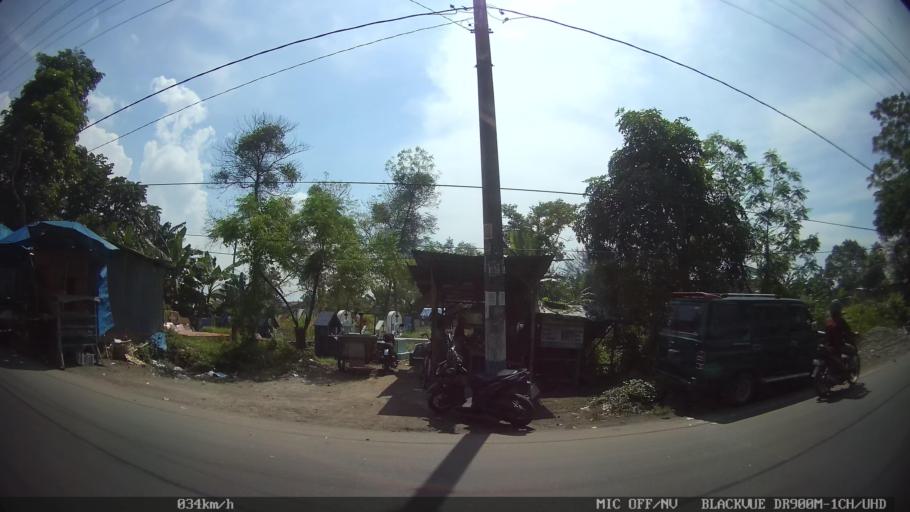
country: ID
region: North Sumatra
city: Medan
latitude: 3.6383
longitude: 98.6574
